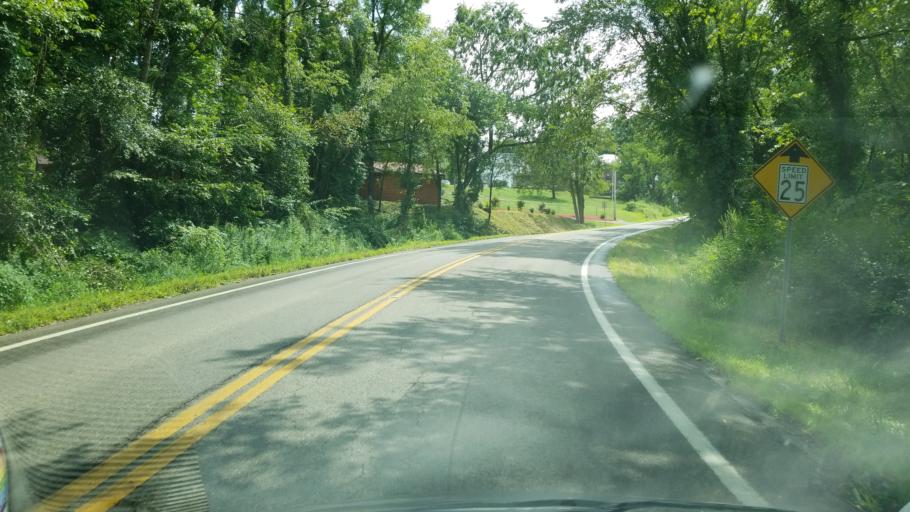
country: US
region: Ohio
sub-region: Tuscarawas County
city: Sugarcreek
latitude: 40.5433
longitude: -81.7197
